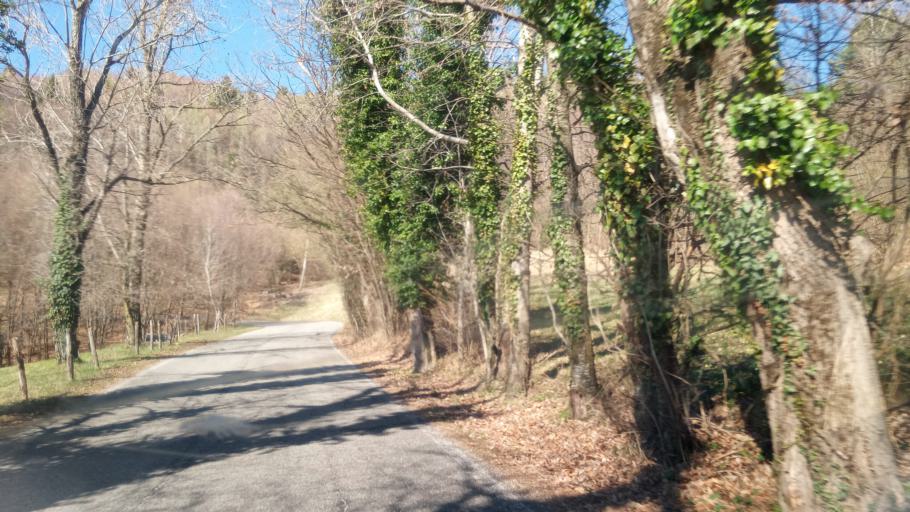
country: IT
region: Veneto
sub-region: Provincia di Treviso
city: Borso del Grappa
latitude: 45.8217
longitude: 11.7637
